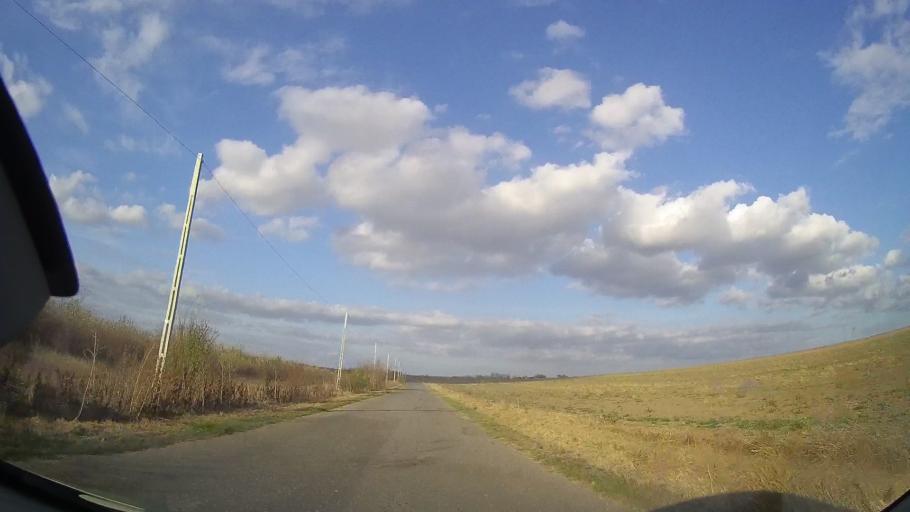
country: RO
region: Constanta
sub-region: Comuna Cerchezu
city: Cerchezu
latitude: 43.8471
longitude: 28.0989
